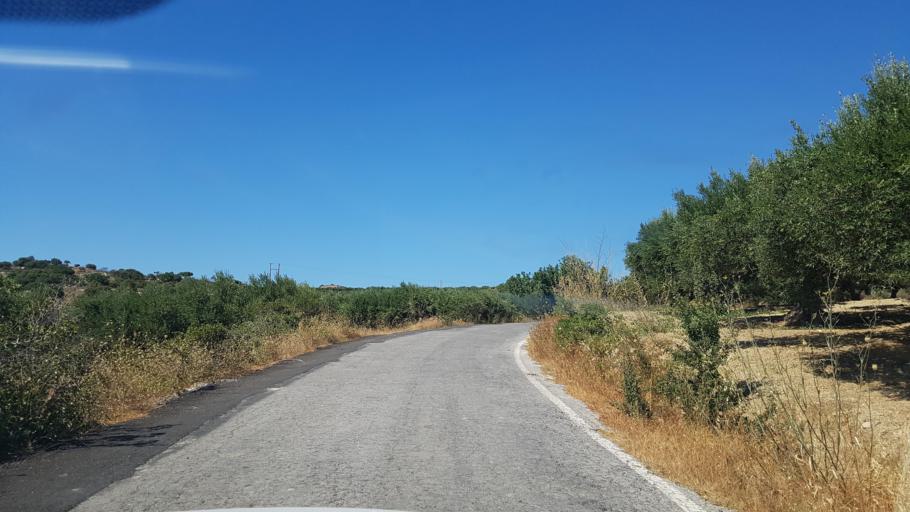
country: GR
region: Crete
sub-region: Nomos Chanias
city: Kolympari
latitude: 35.5014
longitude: 23.7269
